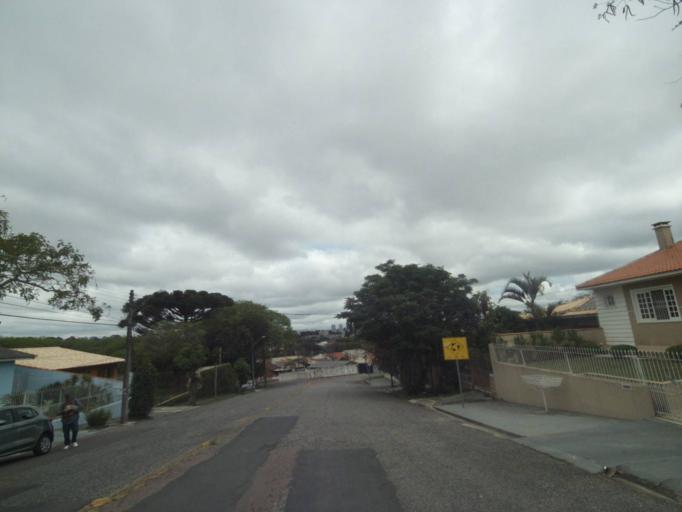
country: BR
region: Parana
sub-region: Pinhais
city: Pinhais
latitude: -25.3986
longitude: -49.2168
